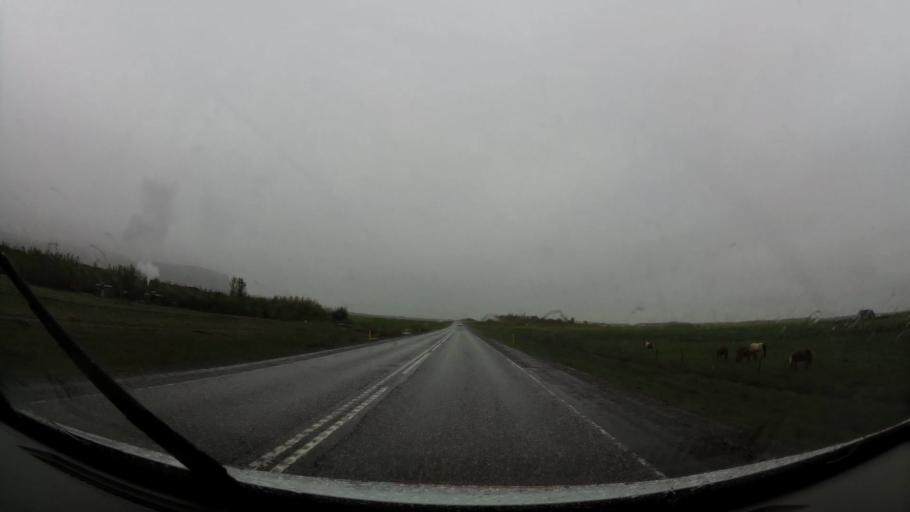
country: IS
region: South
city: Hveragerdi
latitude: 63.9765
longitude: -21.1469
